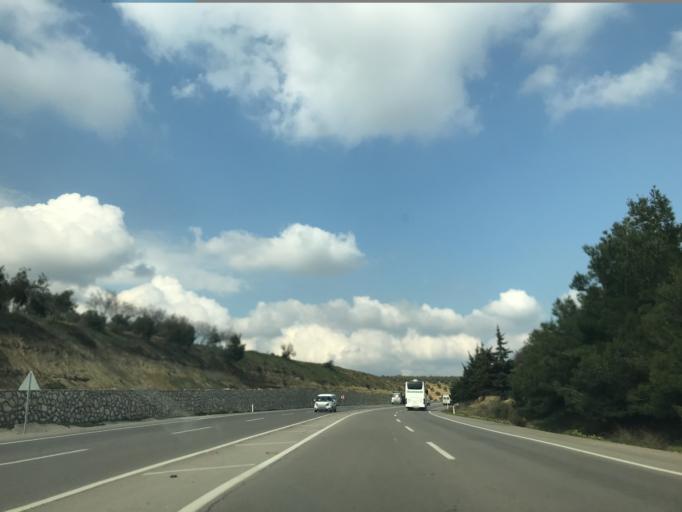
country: TR
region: Hatay
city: Kirikhan
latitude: 36.4695
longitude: 36.2844
